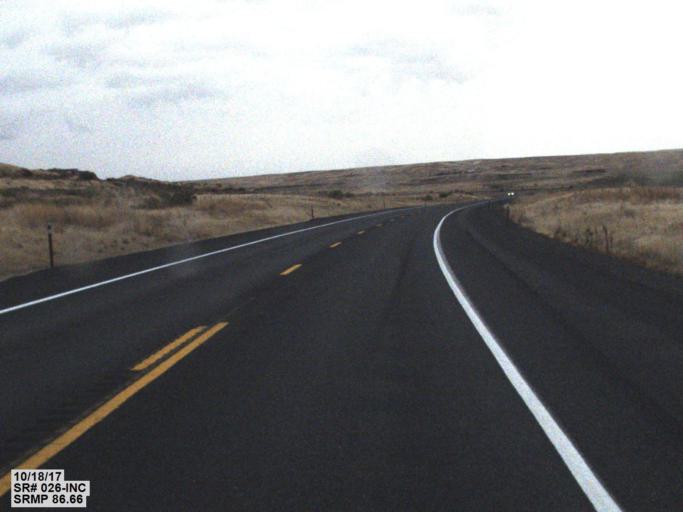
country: US
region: Washington
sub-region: Adams County
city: Ritzville
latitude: 46.7446
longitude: -118.2363
